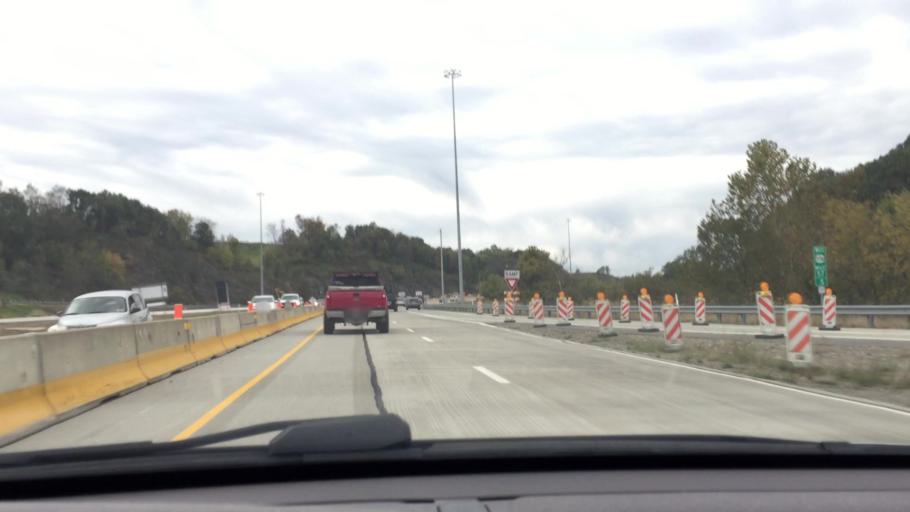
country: US
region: Pennsylvania
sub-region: Allegheny County
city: Enlow
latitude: 40.4685
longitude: -80.2020
